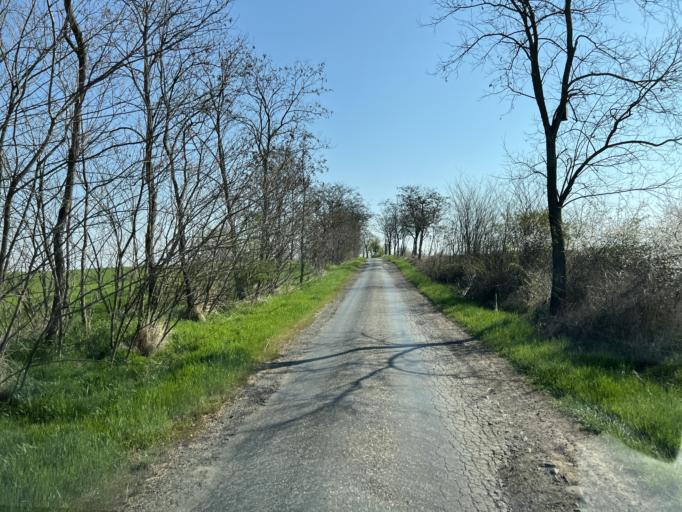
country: SK
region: Nitriansky
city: Sahy
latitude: 48.0486
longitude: 18.8572
